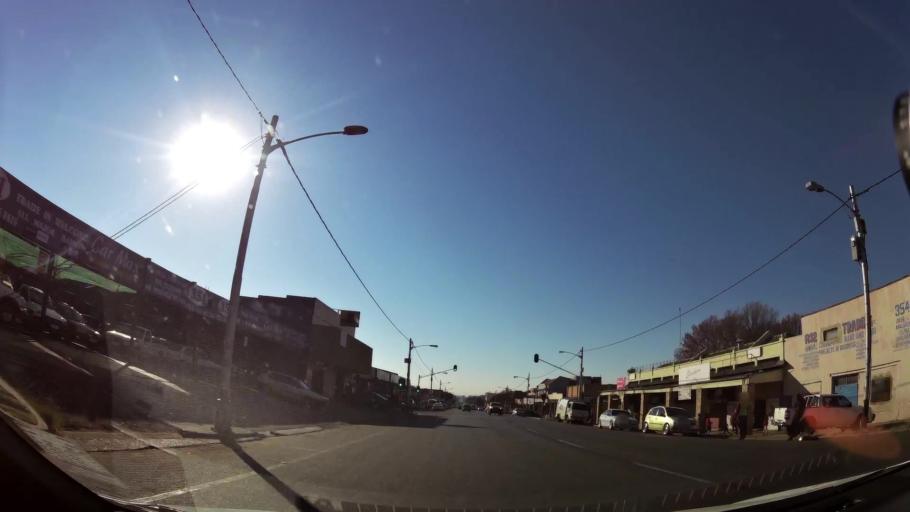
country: ZA
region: Gauteng
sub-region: City of Johannesburg Metropolitan Municipality
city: Johannesburg
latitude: -26.2036
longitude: 28.0961
